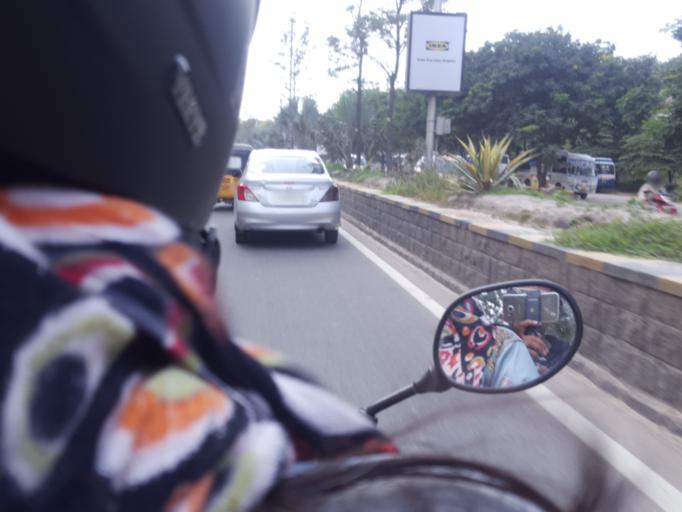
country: IN
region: Telangana
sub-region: Rangareddi
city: Kukatpalli
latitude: 17.4214
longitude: 78.3842
